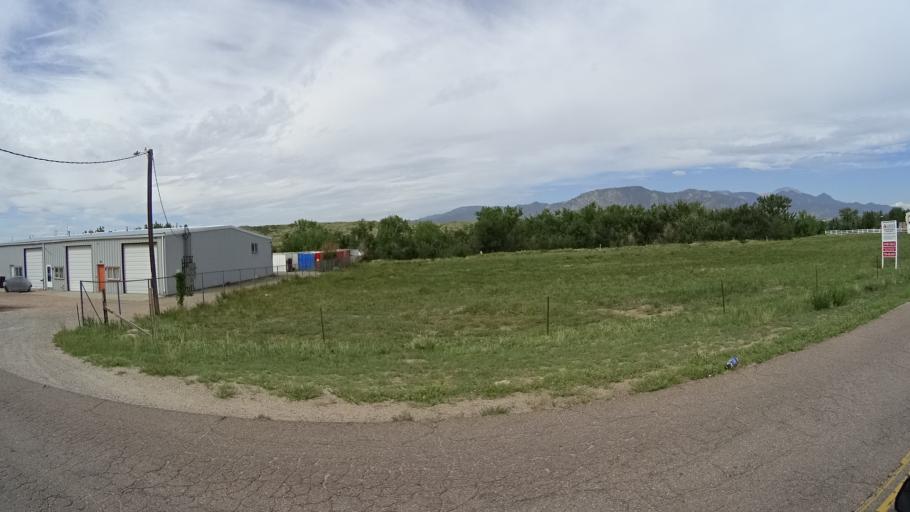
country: US
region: Colorado
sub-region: El Paso County
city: Security-Widefield
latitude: 38.7419
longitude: -104.7393
